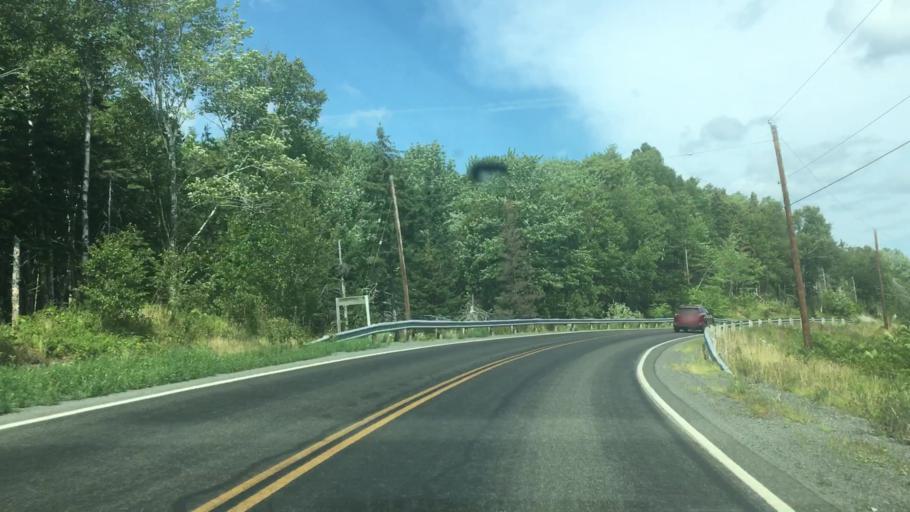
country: CA
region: Nova Scotia
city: Sydney Mines
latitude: 46.2142
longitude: -60.6202
